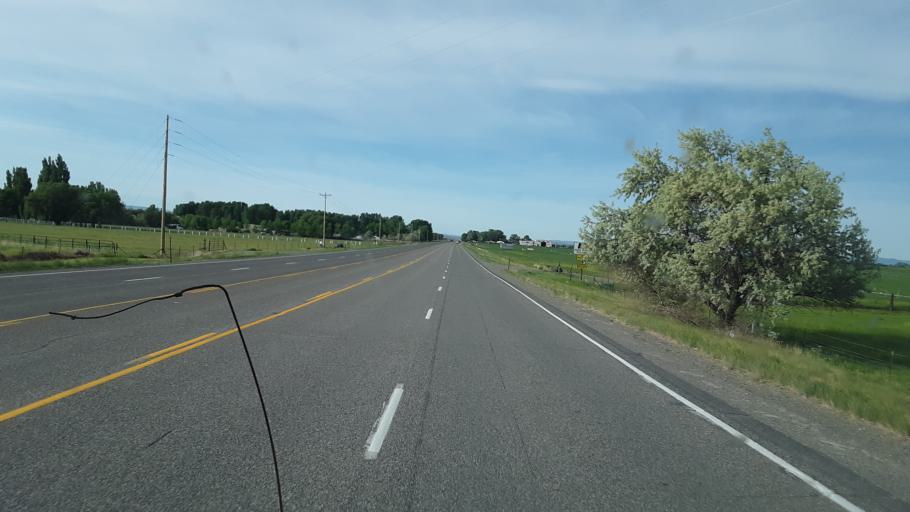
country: US
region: Wyoming
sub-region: Fremont County
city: Riverton
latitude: 43.0783
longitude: -108.3811
